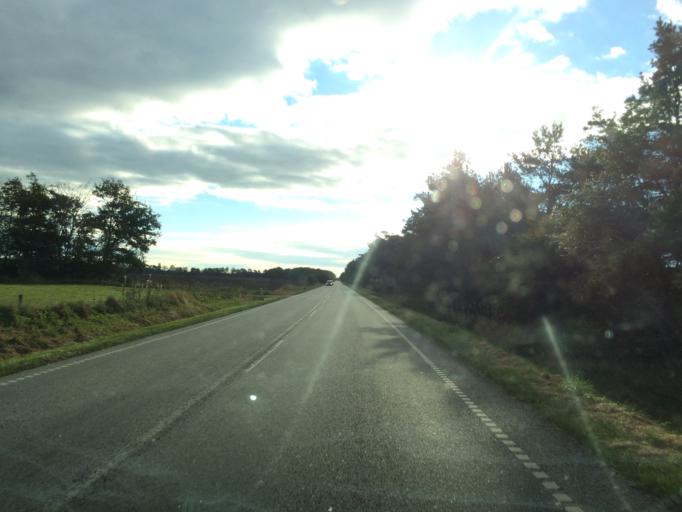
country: DK
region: Central Jutland
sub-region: Herning Kommune
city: Kibaek
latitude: 55.9490
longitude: 8.7422
